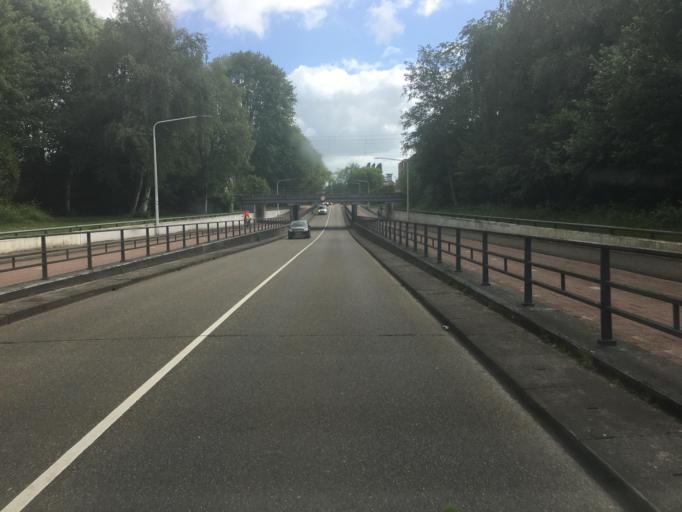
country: NL
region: Friesland
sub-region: Gemeente Heerenveen
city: Heerenveen
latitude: 52.9544
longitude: 5.9212
